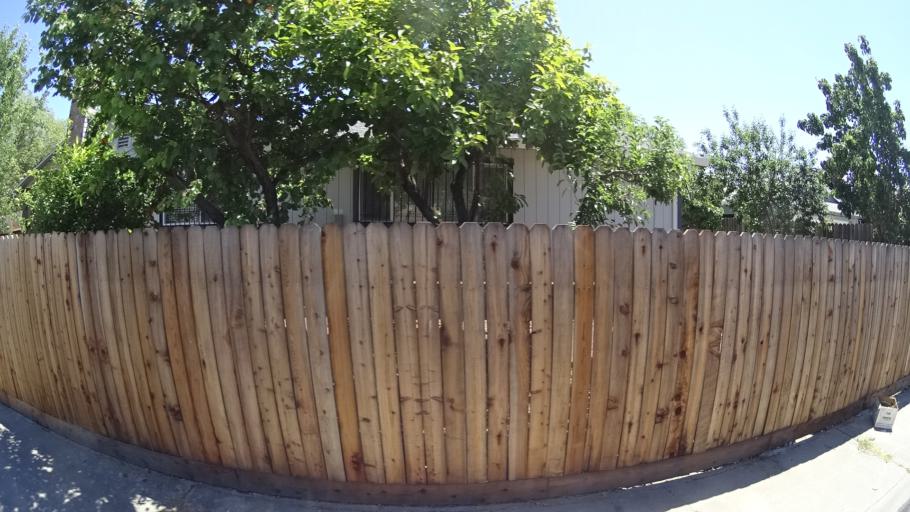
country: US
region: California
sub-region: Sacramento County
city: Florin
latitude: 38.5135
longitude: -121.4206
